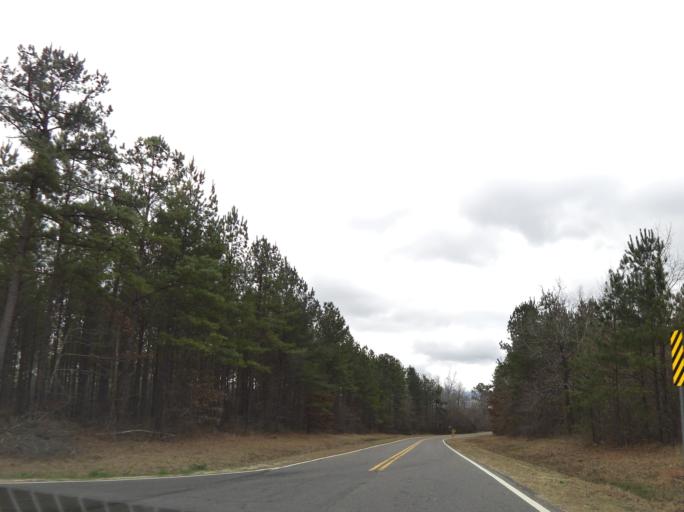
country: US
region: Georgia
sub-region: Bleckley County
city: Cochran
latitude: 32.5094
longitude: -83.3677
